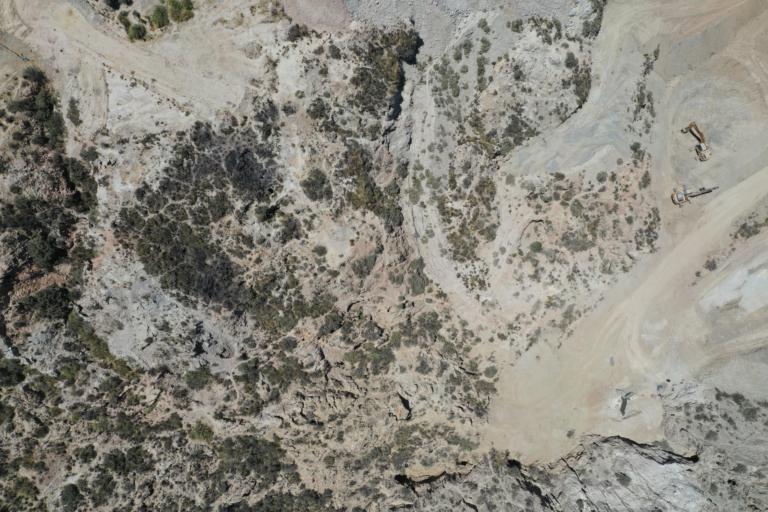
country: BO
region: La Paz
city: La Paz
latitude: -16.5555
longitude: -68.1303
